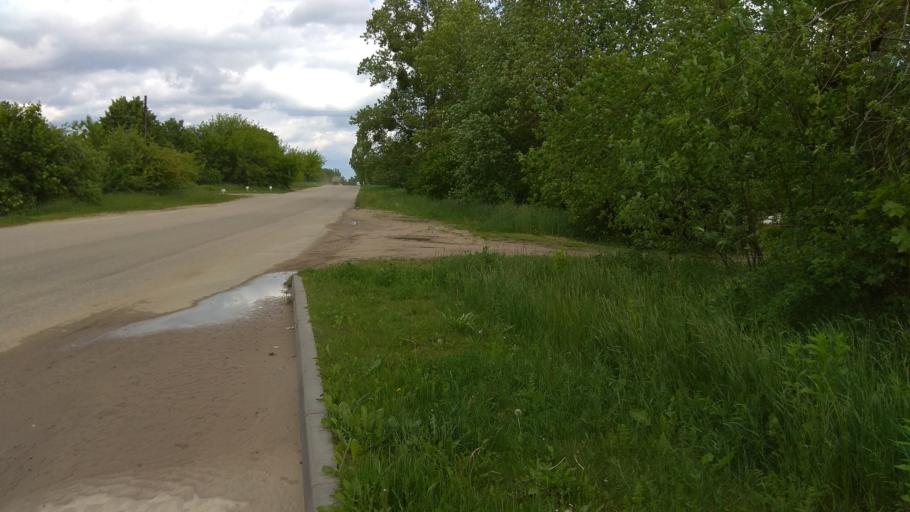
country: BY
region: Grodnenskaya
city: Hrodna
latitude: 53.7124
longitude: 23.7971
